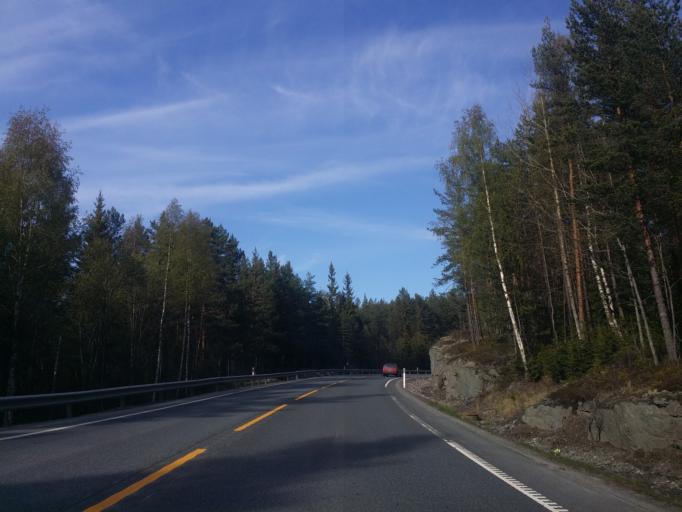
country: NO
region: Telemark
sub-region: Notodden
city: Notodden
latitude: 59.5841
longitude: 9.3002
